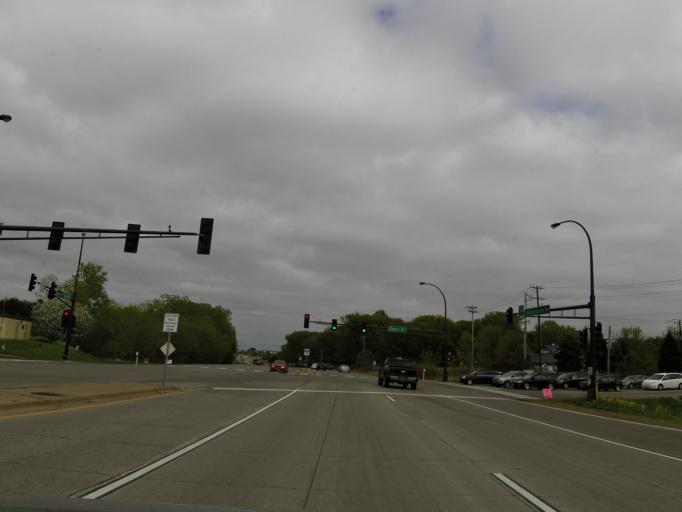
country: US
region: Minnesota
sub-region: Washington County
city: Woodbury
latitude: 44.9201
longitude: -92.9447
